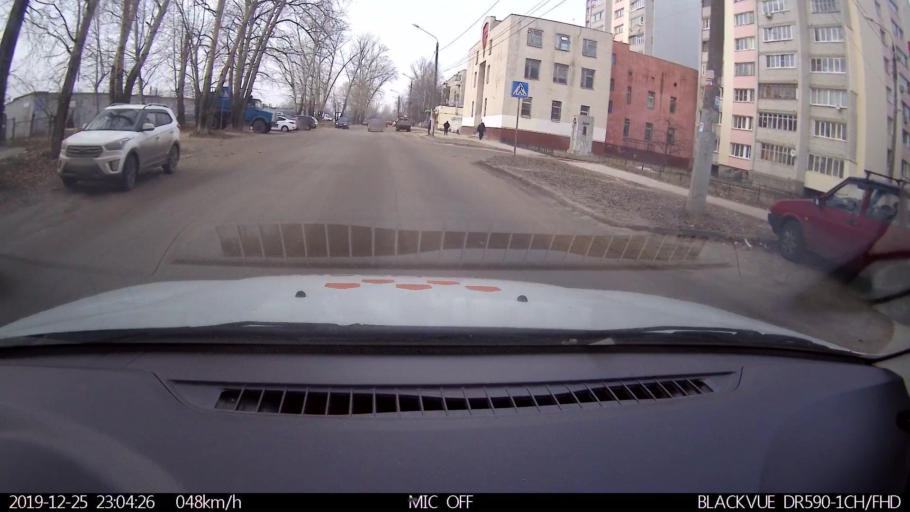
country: RU
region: Nizjnij Novgorod
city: Gorbatovka
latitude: 56.3578
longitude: 43.8101
